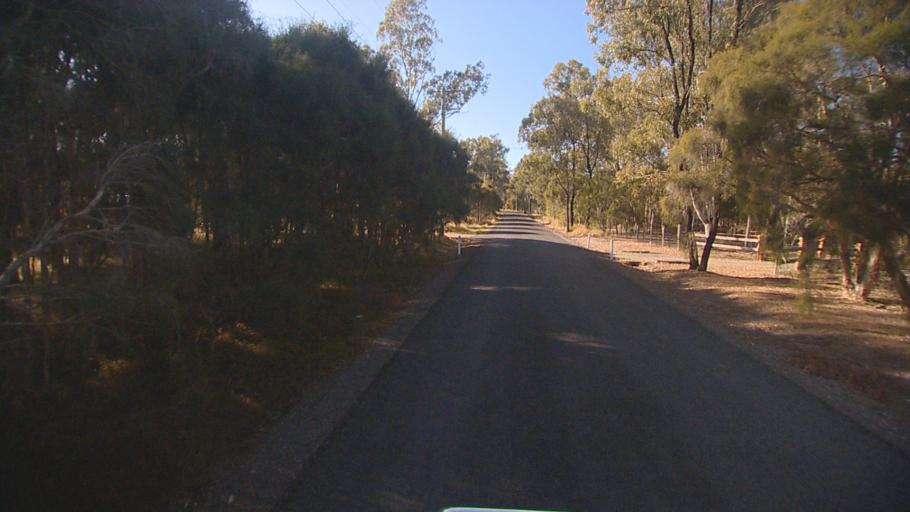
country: AU
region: Queensland
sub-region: Logan
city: Cedar Vale
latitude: -27.8383
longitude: 152.9997
